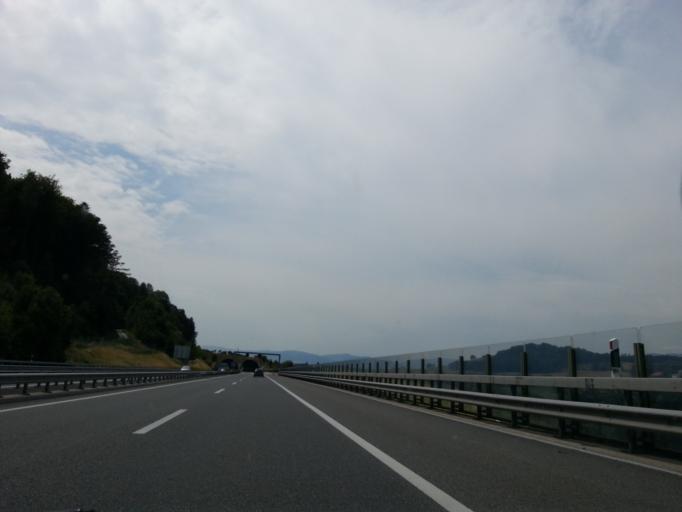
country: CH
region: Vaud
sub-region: Jura-Nord vaudois District
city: Yvonand
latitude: 46.7673
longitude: 6.7007
